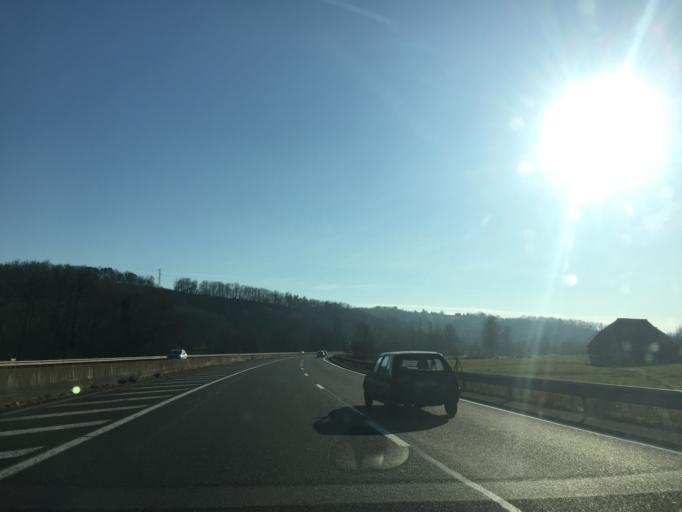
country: FR
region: Limousin
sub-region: Departement de la Correze
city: Ussac
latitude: 45.2111
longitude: 1.5158
